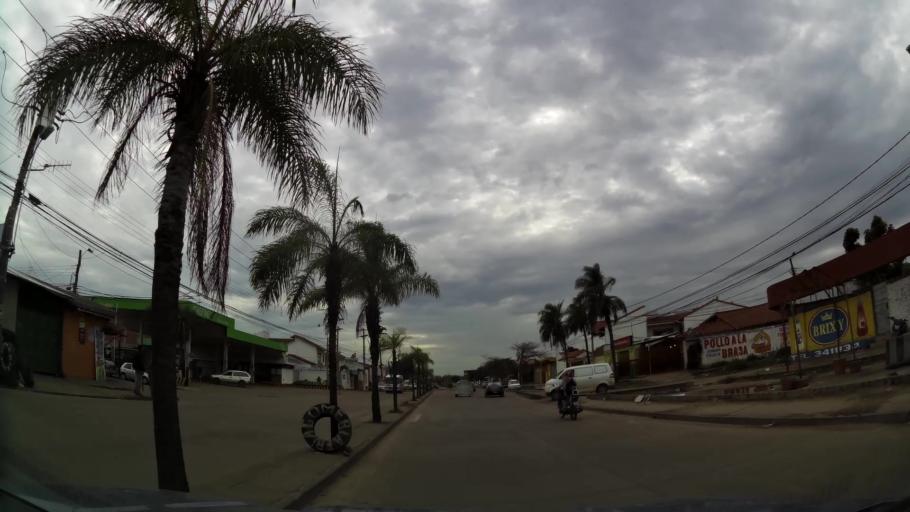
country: BO
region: Santa Cruz
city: Santa Cruz de la Sierra
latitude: -17.7607
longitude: -63.1579
